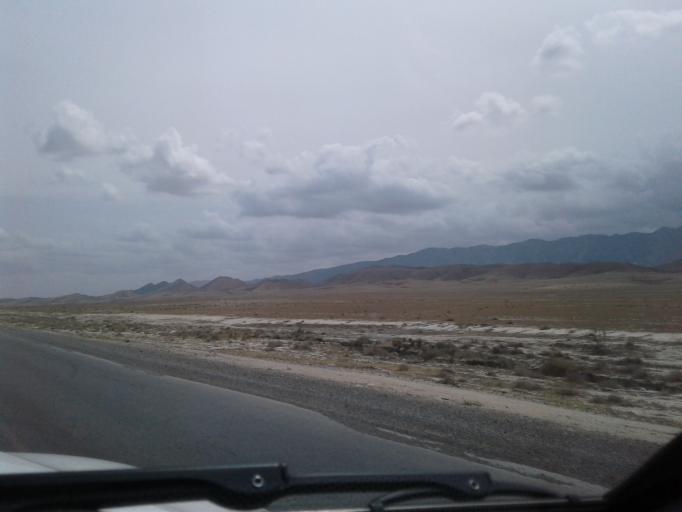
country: IR
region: Razavi Khorasan
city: Dargaz
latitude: 37.7103
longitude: 59.0269
